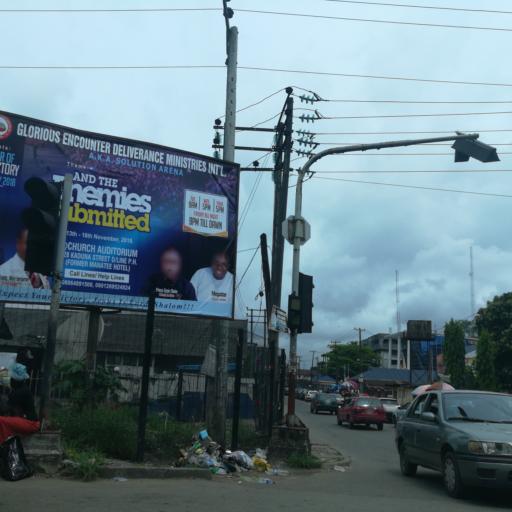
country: NG
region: Rivers
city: Port Harcourt
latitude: 4.7890
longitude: 7.0033
